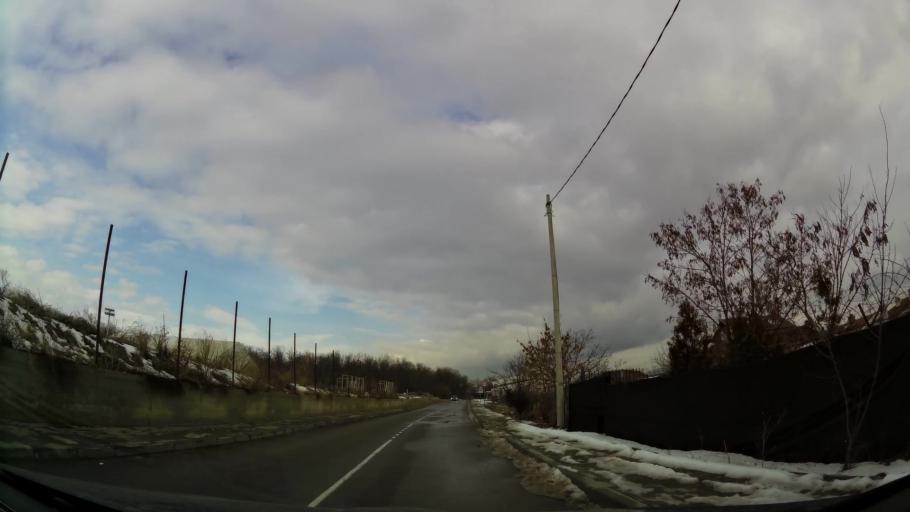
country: XK
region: Pristina
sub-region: Komuna e Prishtines
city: Pristina
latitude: 42.6663
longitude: 21.1513
